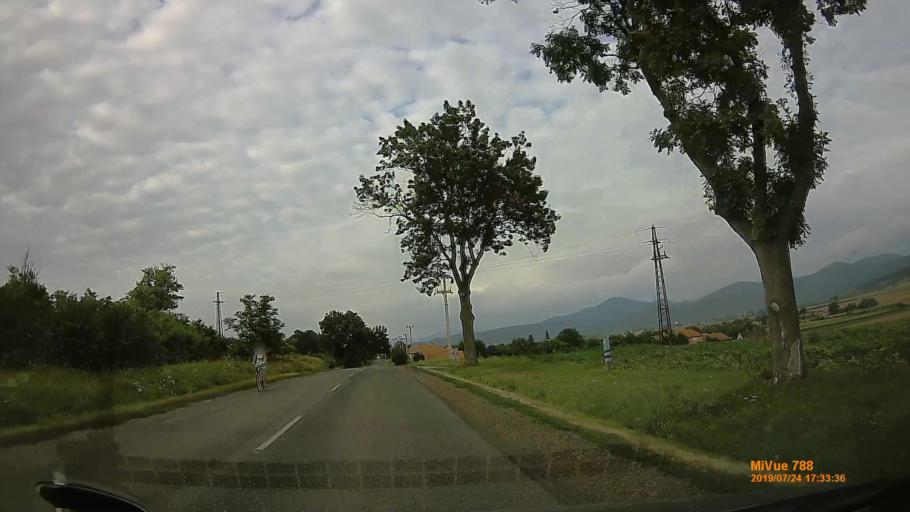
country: HU
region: Borsod-Abauj-Zemplen
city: Abaujszanto
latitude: 48.2958
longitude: 21.1923
